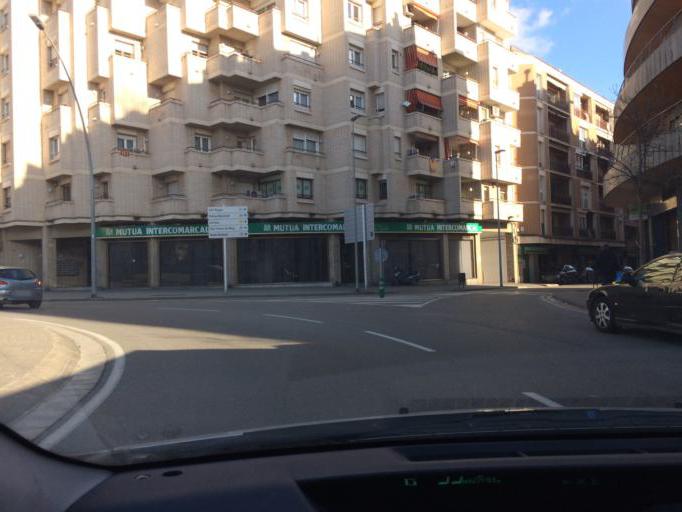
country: ES
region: Catalonia
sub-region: Provincia de Barcelona
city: Manresa
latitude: 41.7347
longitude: 1.8238
